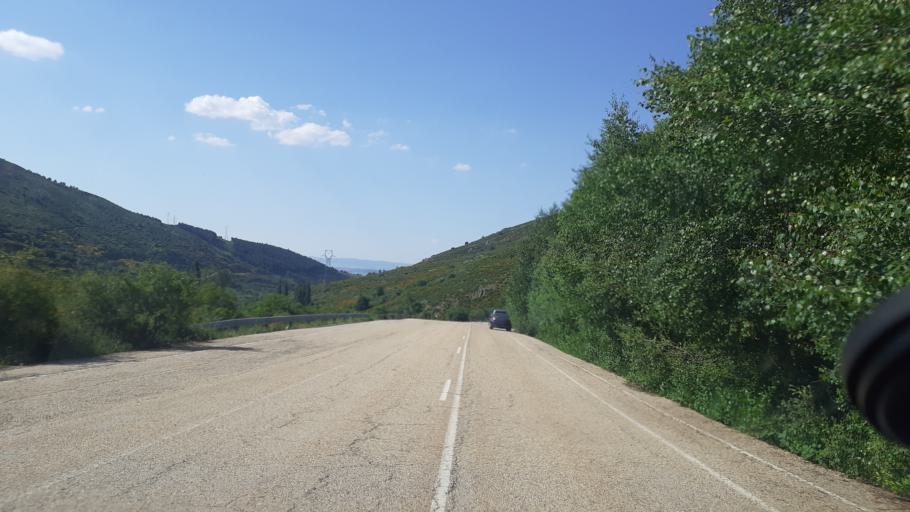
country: ES
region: Madrid
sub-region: Provincia de Madrid
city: Somosierra
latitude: 41.1434
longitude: -3.5781
